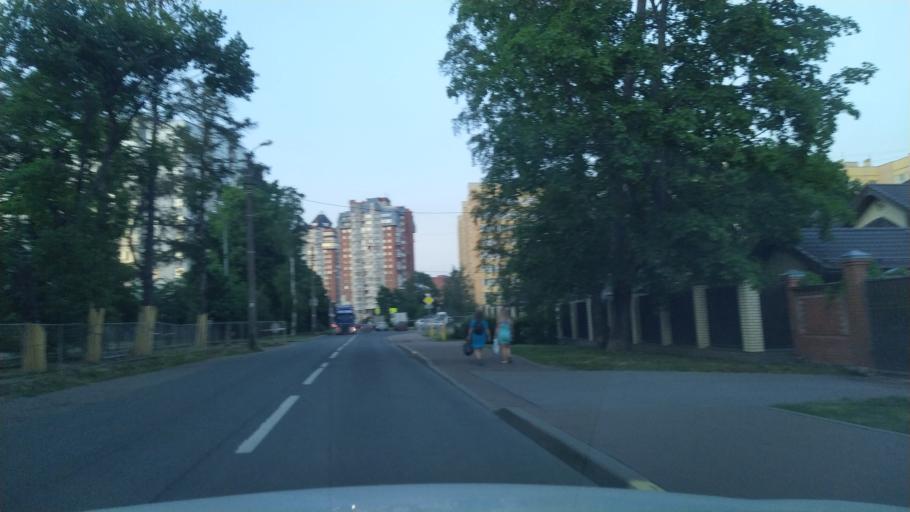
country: RU
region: St.-Petersburg
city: Sestroretsk
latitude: 60.0903
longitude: 29.9453
